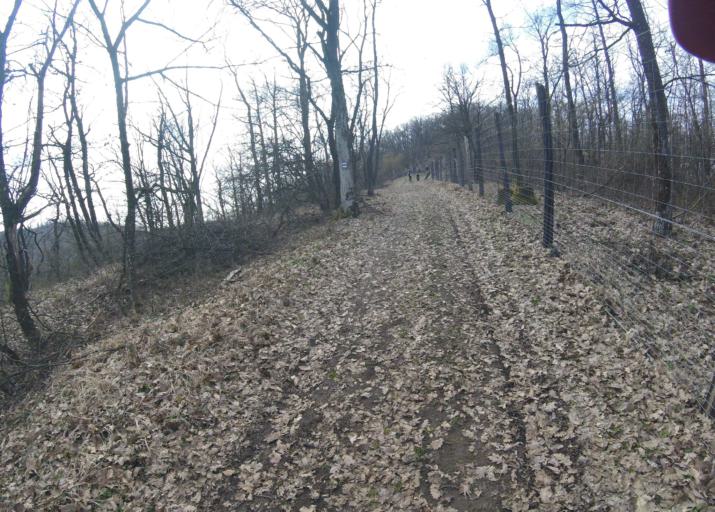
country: HU
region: Heves
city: Belapatfalva
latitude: 48.0093
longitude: 20.3412
